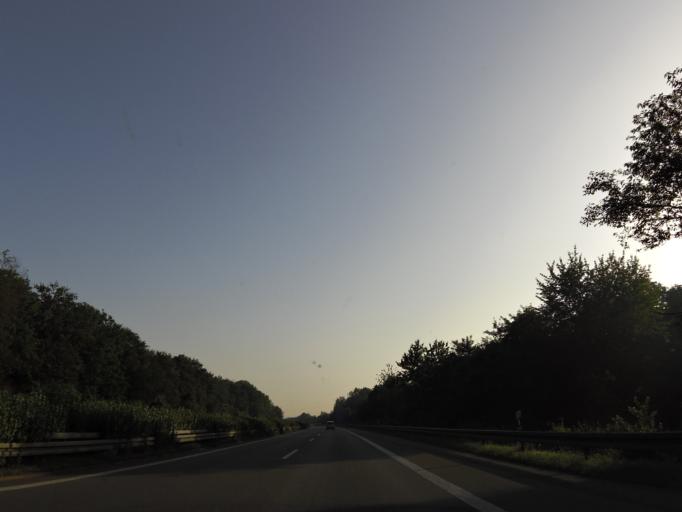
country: DE
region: Bavaria
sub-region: Swabia
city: Nersingen
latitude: 48.4438
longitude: 10.1138
